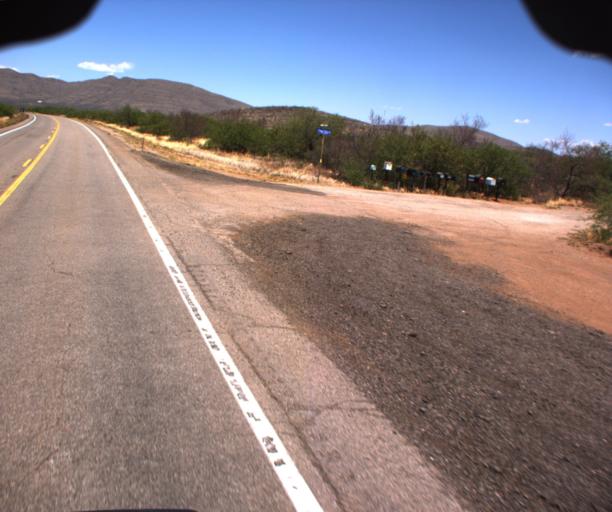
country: US
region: Arizona
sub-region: Cochise County
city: Bisbee
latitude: 31.5438
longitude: -110.0104
